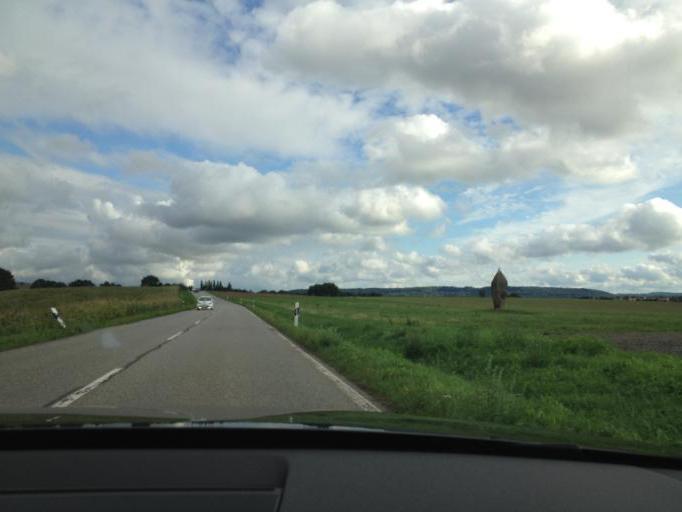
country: DE
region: Saarland
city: Sankt Wendel
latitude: 49.4857
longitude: 7.1643
